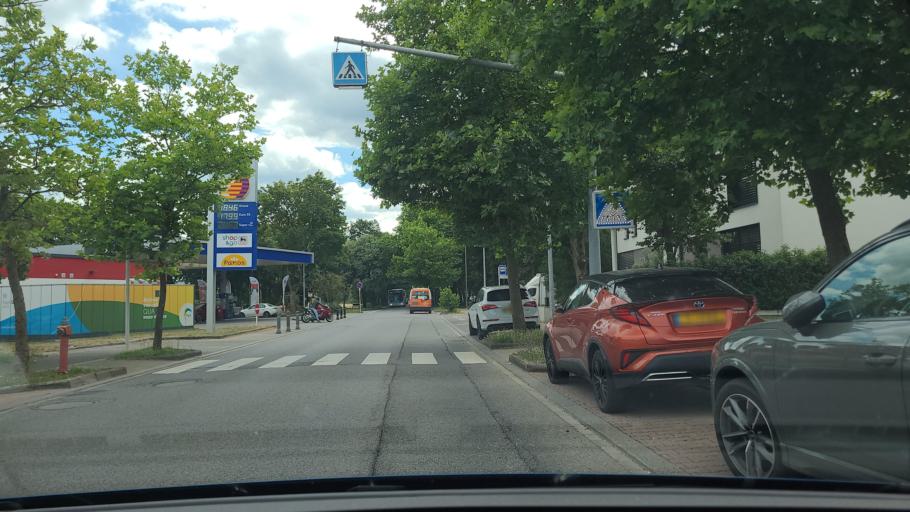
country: LU
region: Luxembourg
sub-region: Canton d'Esch-sur-Alzette
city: Bettembourg
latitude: 49.5260
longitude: 6.1009
